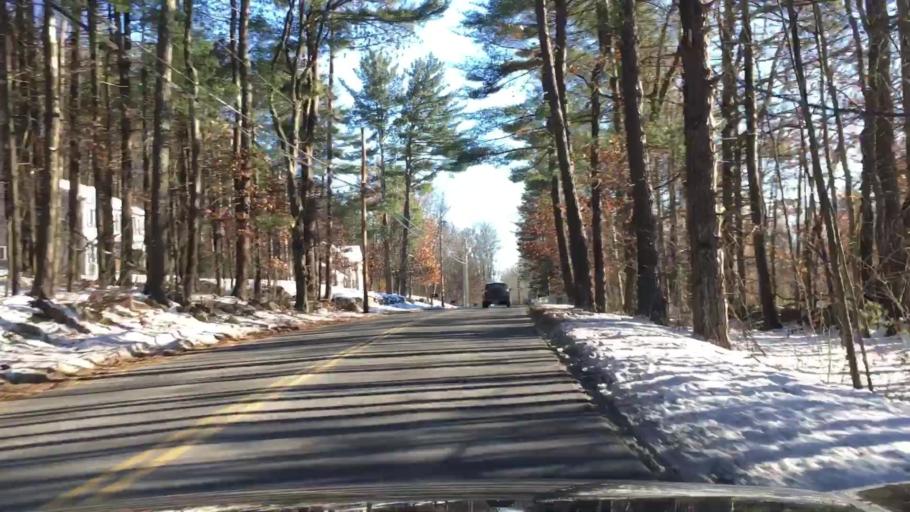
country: US
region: New Hampshire
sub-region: Hillsborough County
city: Milford
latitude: 42.8339
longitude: -71.5926
